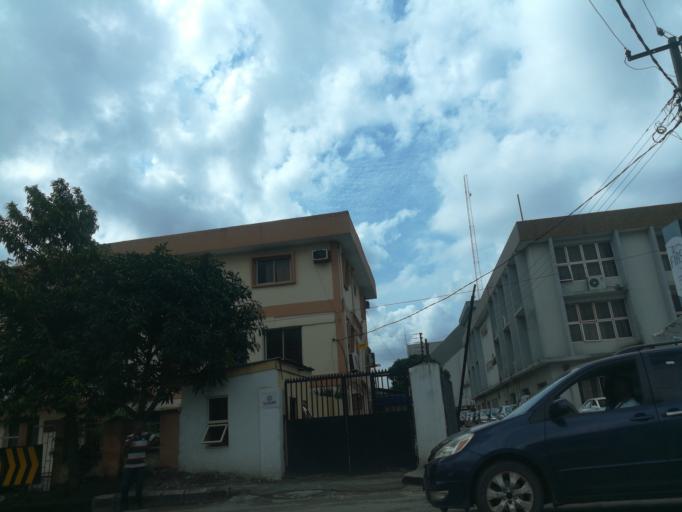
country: NG
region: Lagos
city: Somolu
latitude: 6.5453
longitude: 3.3589
